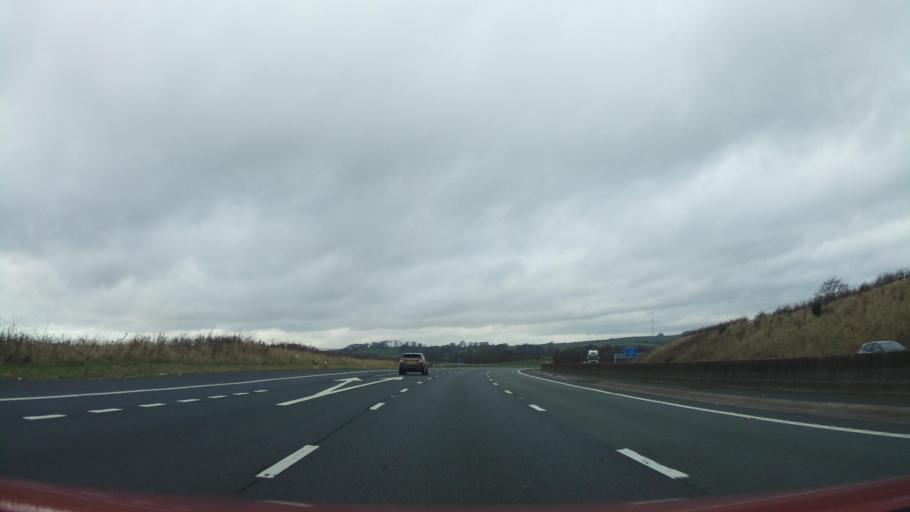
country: GB
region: England
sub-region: Lancashire
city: Bolton le Sands
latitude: 54.0603
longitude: -2.7702
